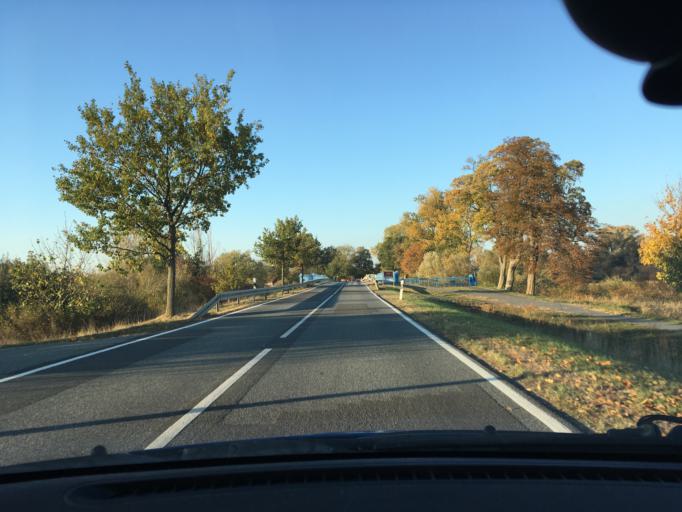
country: DE
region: Lower Saxony
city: Bleckede
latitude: 53.3380
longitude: 10.7977
